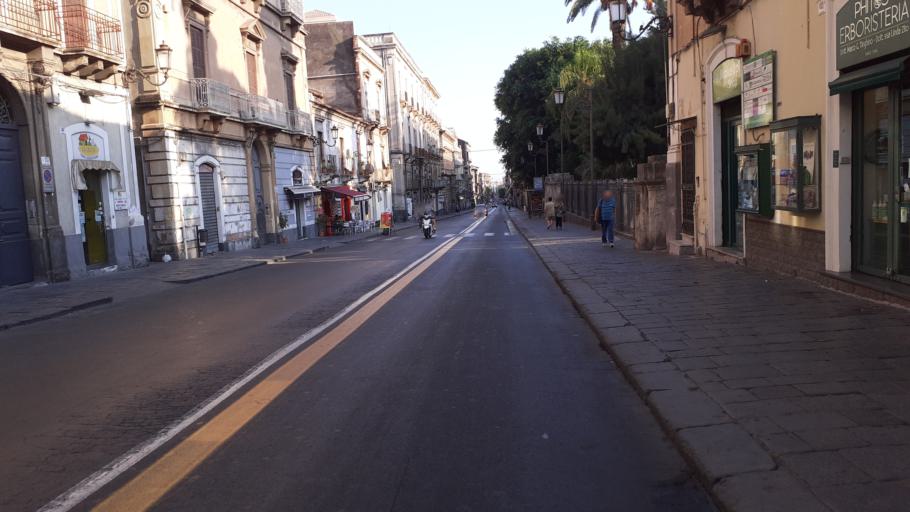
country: IT
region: Sicily
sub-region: Catania
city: Catania
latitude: 37.5162
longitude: 15.0841
